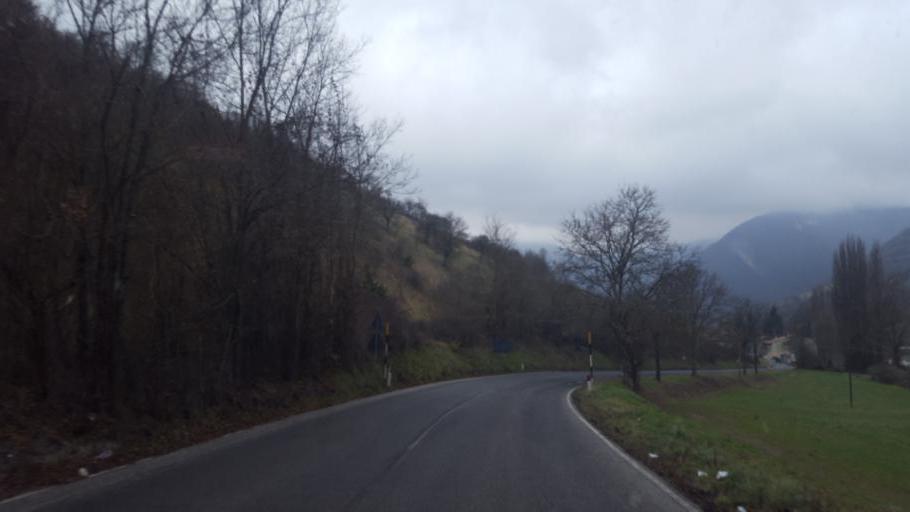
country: IT
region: The Marches
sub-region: Provincia di Macerata
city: Visso
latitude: 42.9485
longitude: 13.0840
